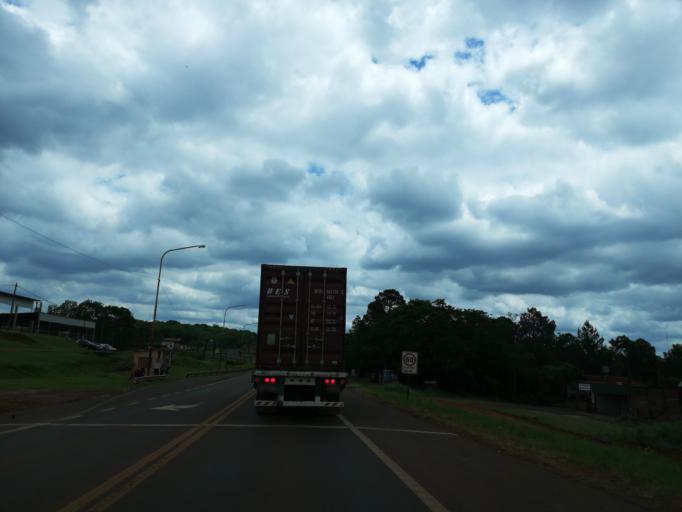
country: AR
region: Misiones
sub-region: Departamento de Leandro N. Alem
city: Leandro N. Alem
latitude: -27.6156
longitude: -55.3167
